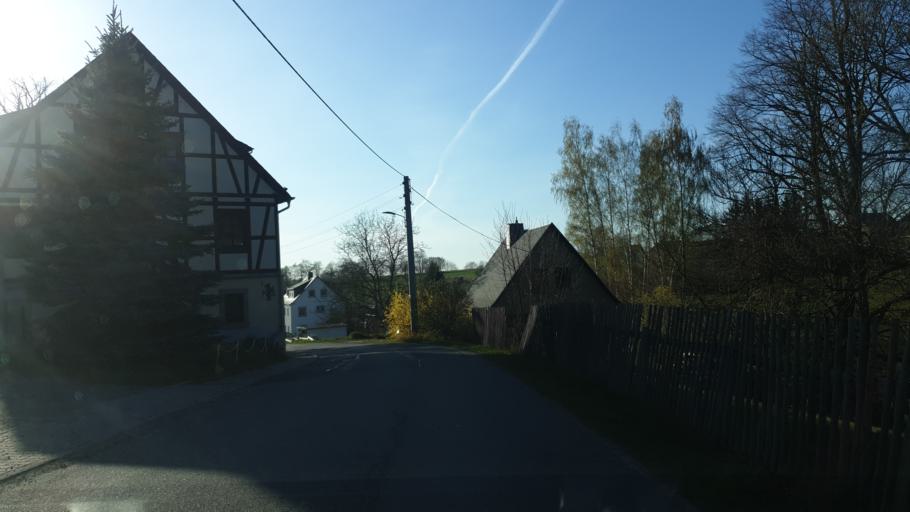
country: DE
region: Saxony
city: Kirchberg
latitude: 50.7617
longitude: 12.7683
